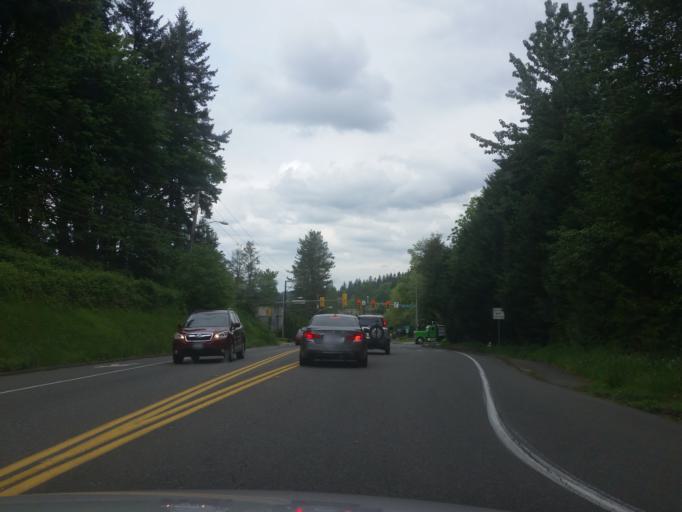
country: US
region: Washington
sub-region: King County
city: Inglewood-Finn Hill
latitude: 47.7320
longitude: -122.2078
